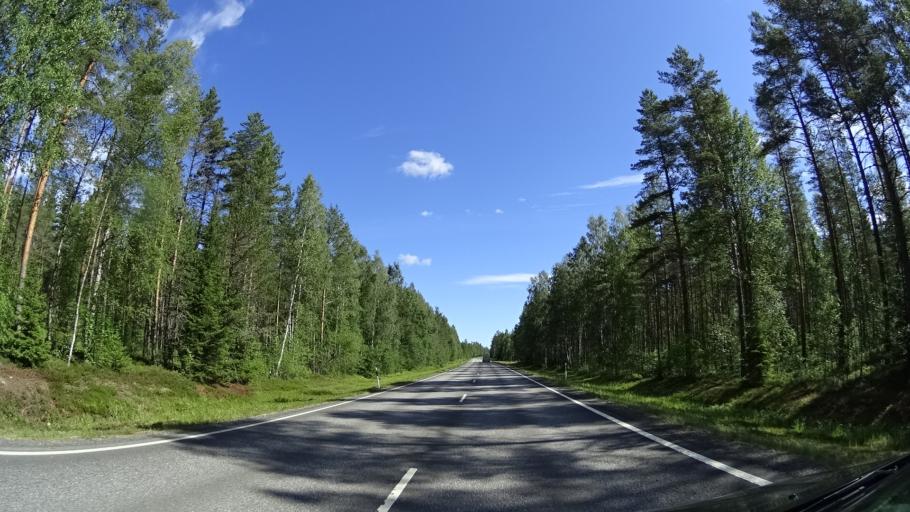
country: FI
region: Pirkanmaa
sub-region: Luoteis-Pirkanmaa
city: Kihnioe
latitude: 62.2253
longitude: 23.2884
